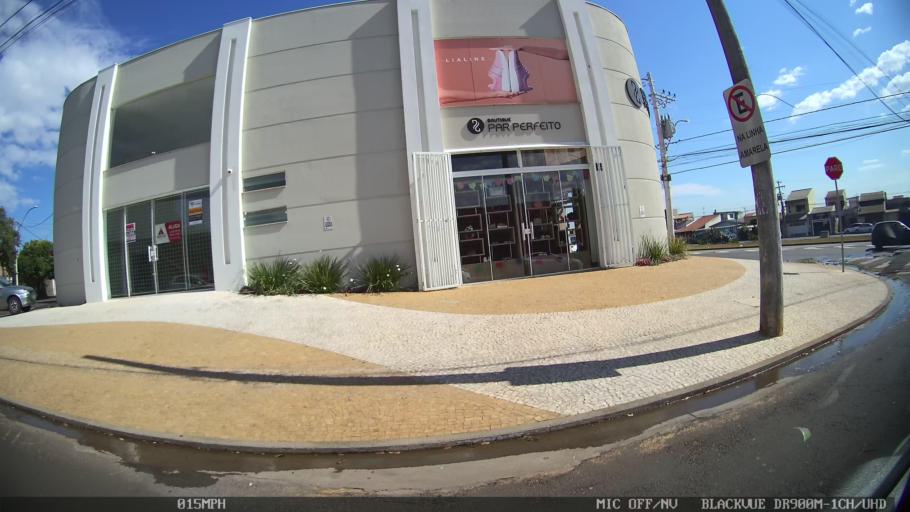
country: BR
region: Sao Paulo
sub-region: Americana
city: Americana
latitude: -22.7394
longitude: -47.3730
